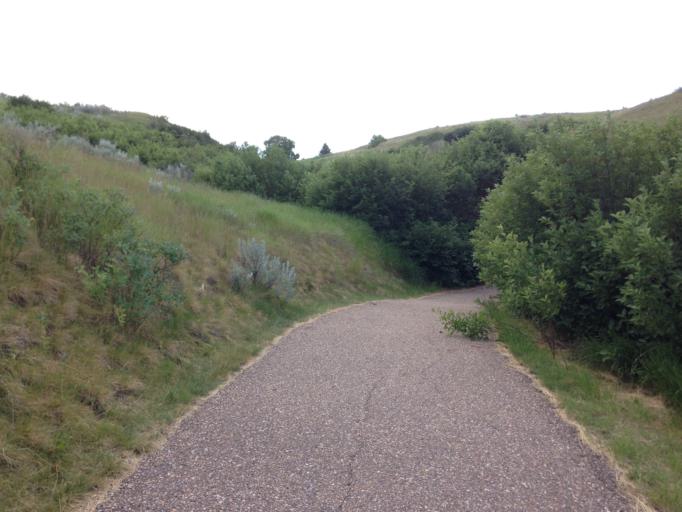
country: CA
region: Alberta
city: Medicine Hat
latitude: 50.0149
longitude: -110.6223
